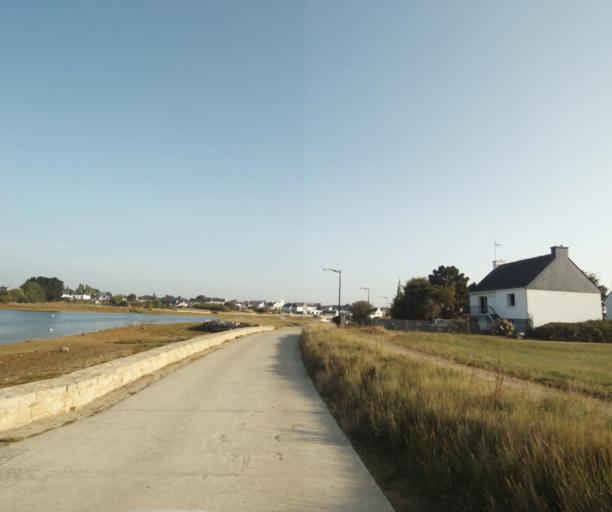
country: FR
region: Brittany
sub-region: Departement du Morbihan
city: Riantec
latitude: 47.7071
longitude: -3.3109
